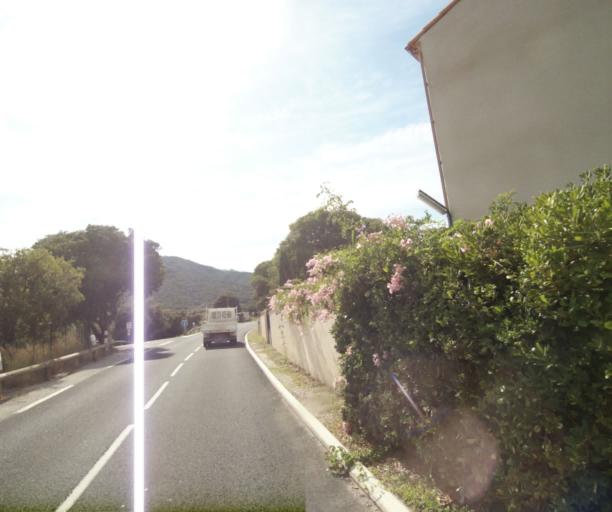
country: FR
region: Languedoc-Roussillon
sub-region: Departement des Pyrenees-Orientales
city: Sant Andreu de Sureda
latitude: 42.5330
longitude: 2.9892
